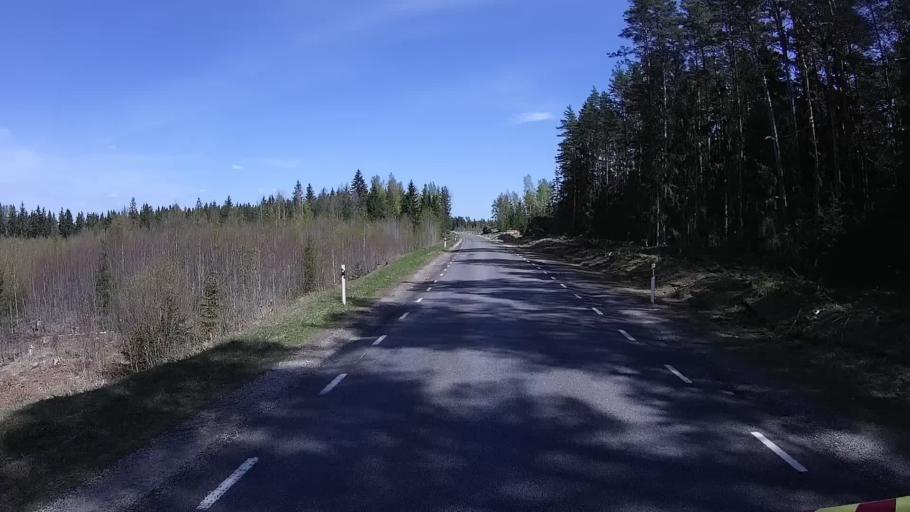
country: EE
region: Harju
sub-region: Nissi vald
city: Turba
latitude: 59.1030
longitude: 24.0308
